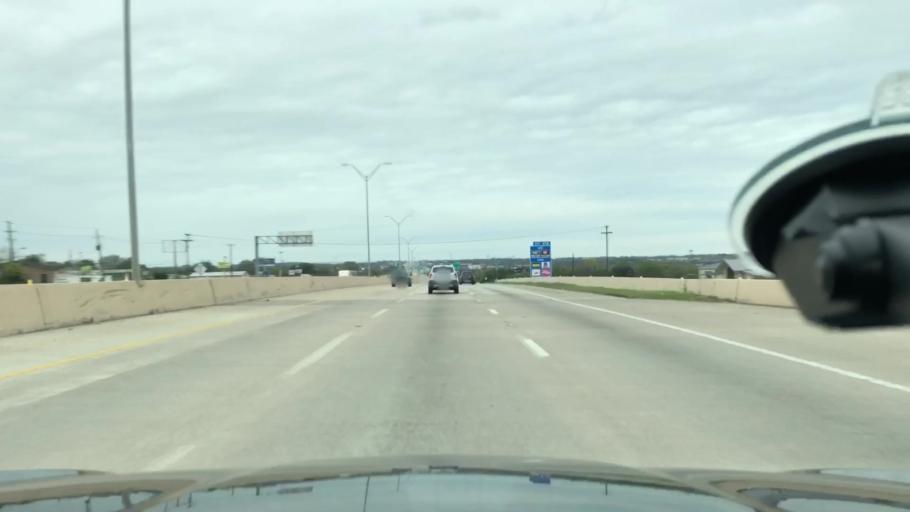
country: US
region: Texas
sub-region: Dallas County
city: DeSoto
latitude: 32.5753
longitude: -96.8223
